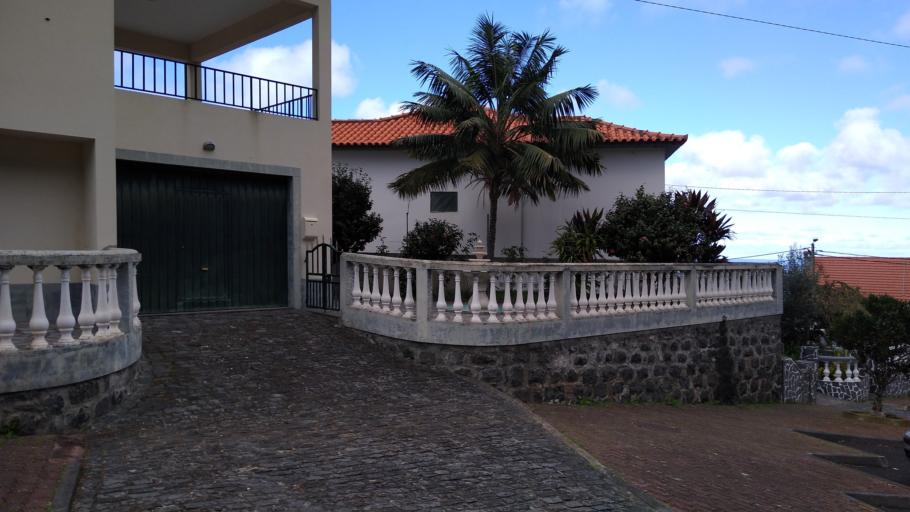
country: PT
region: Madeira
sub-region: Sao Vicente
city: Sao Vicente
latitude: 32.8256
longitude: -16.9884
